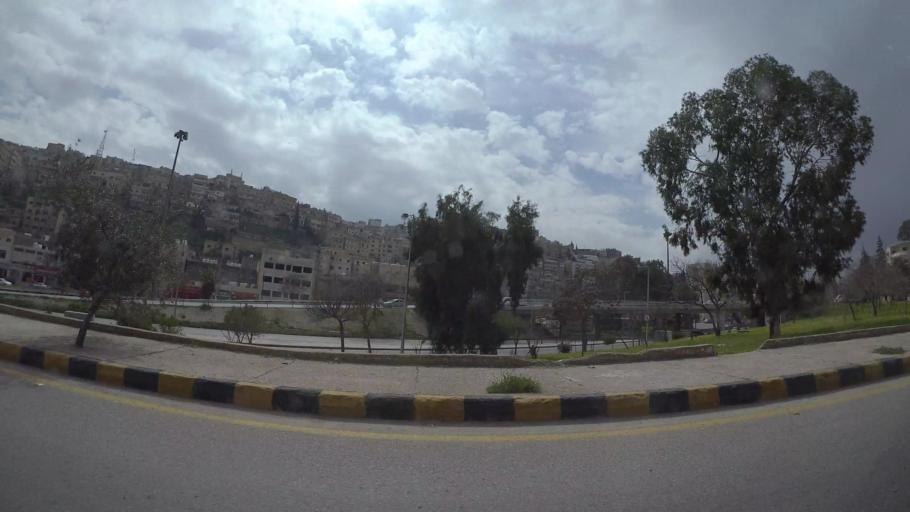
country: JO
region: Amman
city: Amman
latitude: 31.9541
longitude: 35.9460
